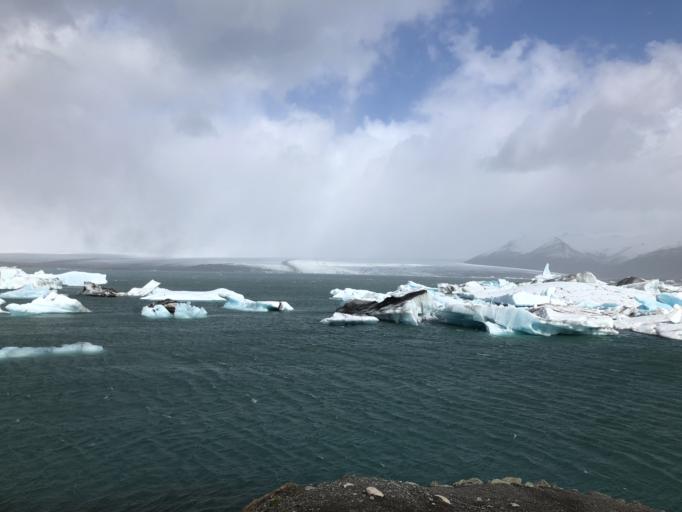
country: IS
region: East
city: Hoefn
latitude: 64.0464
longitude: -16.1834
